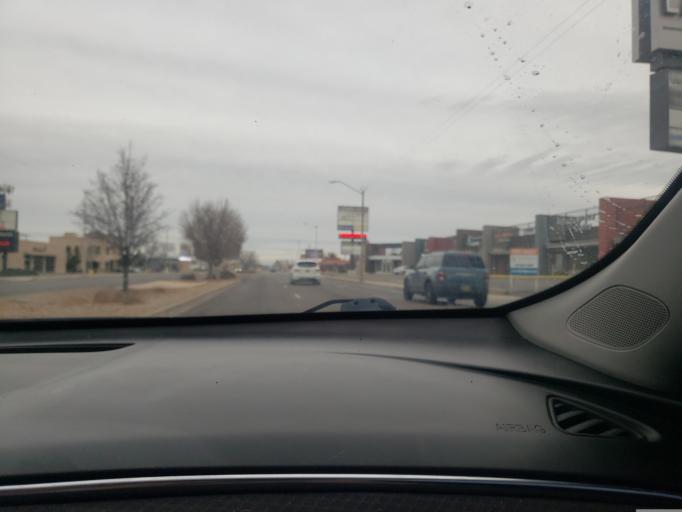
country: US
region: New Mexico
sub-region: Bernalillo County
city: North Valley
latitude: 35.1187
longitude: -106.5865
